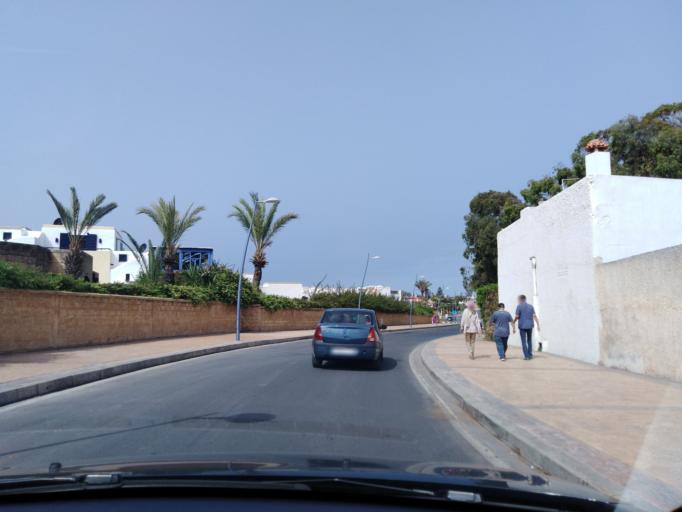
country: MA
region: Doukkala-Abda
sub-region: Safi
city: Safi
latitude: 32.7331
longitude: -9.0384
